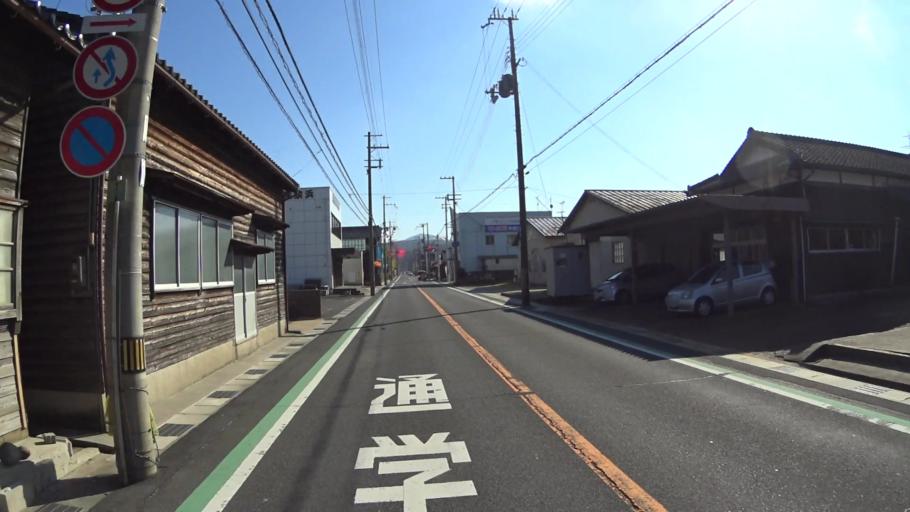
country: JP
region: Kyoto
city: Miyazu
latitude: 35.6759
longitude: 135.0282
